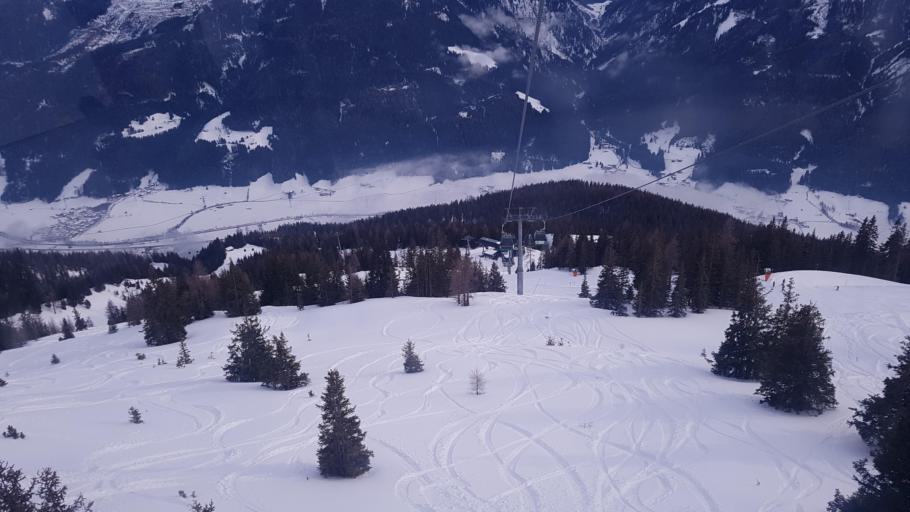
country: AT
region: Salzburg
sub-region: Politischer Bezirk Zell am See
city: Neukirchen am Grossvenediger
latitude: 47.2761
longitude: 12.2998
